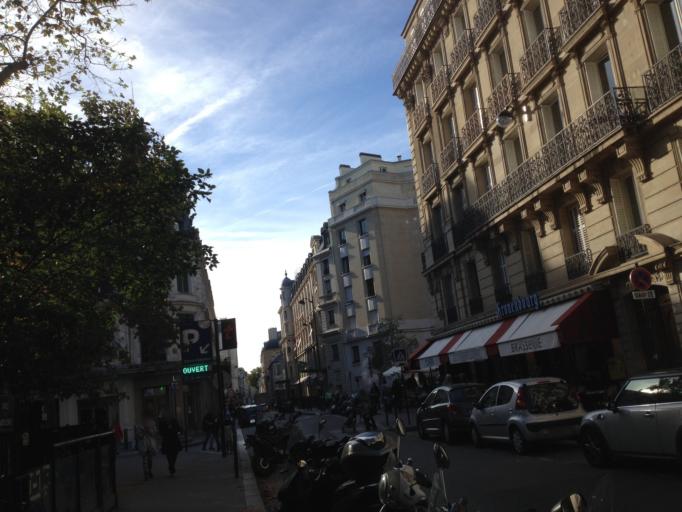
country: FR
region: Ile-de-France
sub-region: Paris
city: Paris
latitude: 48.8518
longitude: 2.3256
